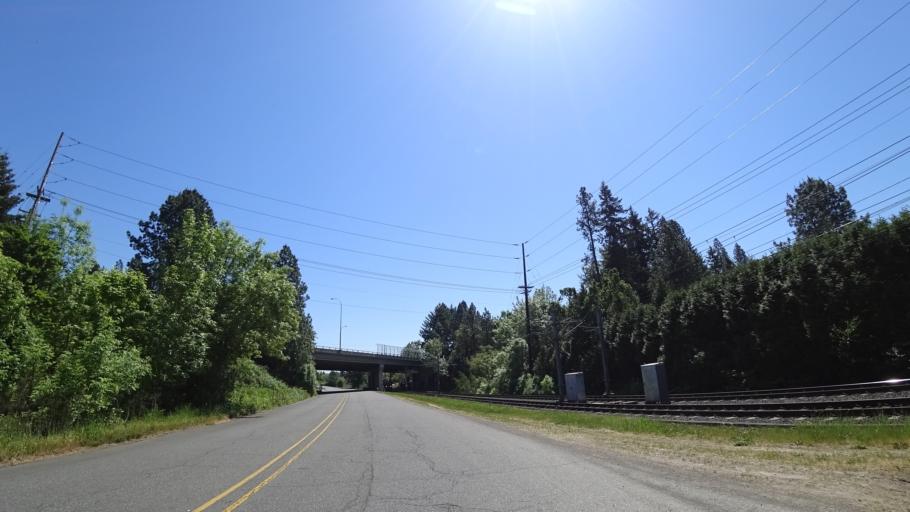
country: US
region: Oregon
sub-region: Washington County
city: Beaverton
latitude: 45.4986
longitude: -122.8293
